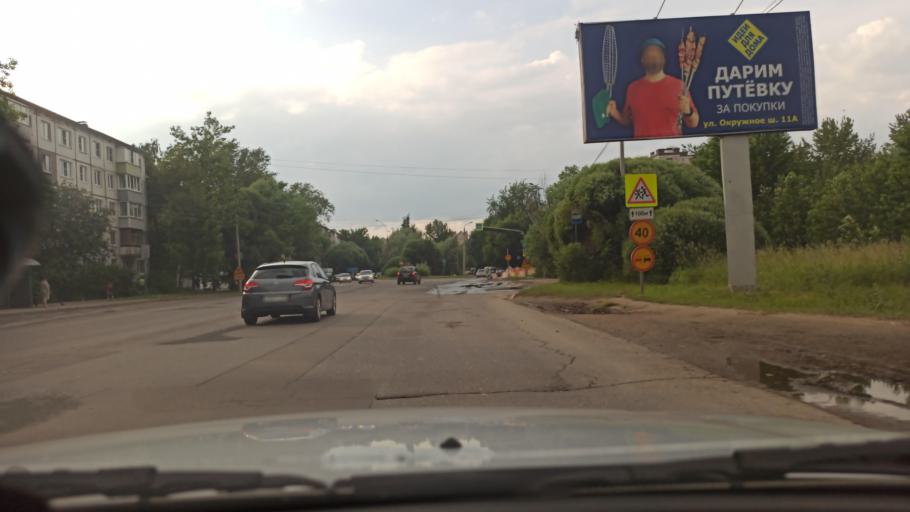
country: RU
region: Vologda
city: Vologda
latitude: 59.2054
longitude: 39.8501
